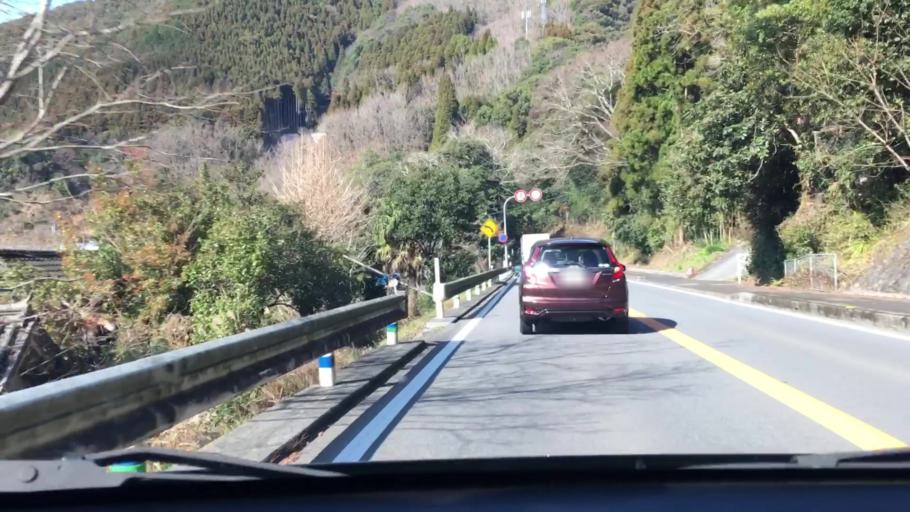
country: JP
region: Oita
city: Saiki
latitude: 32.9936
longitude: 131.8284
